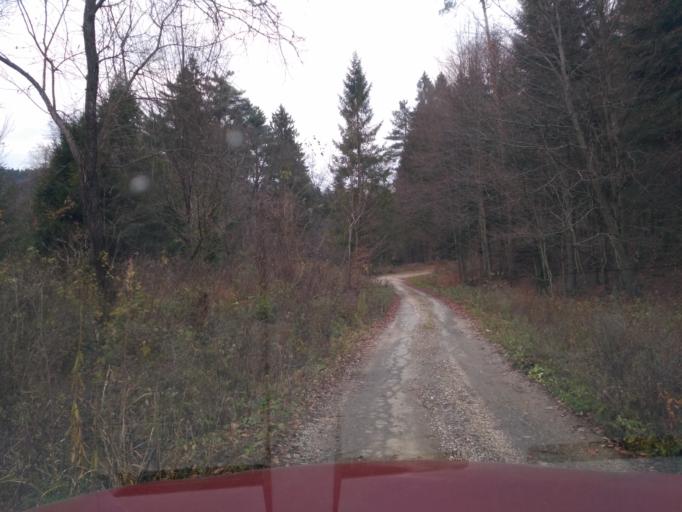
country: SK
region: Kosicky
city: Medzev
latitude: 48.7890
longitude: 20.7603
